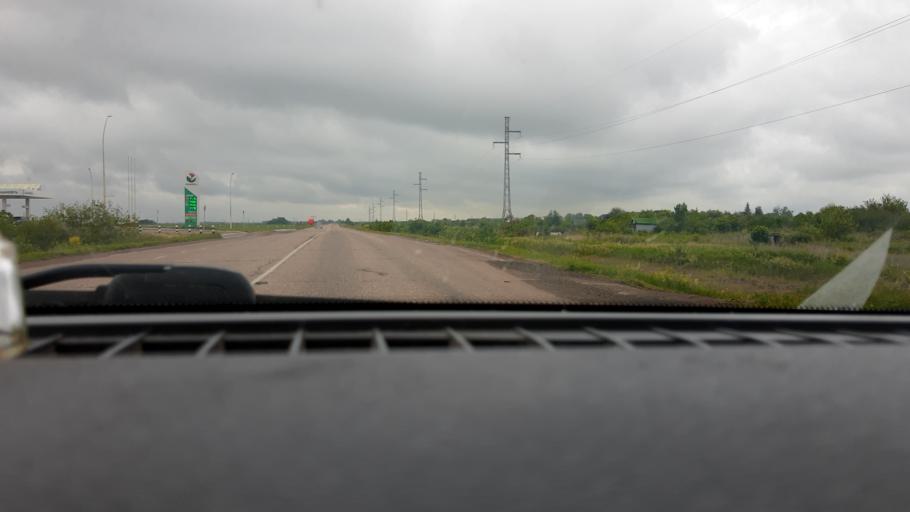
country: RU
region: Bashkortostan
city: Priyutovo
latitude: 53.9158
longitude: 53.9529
